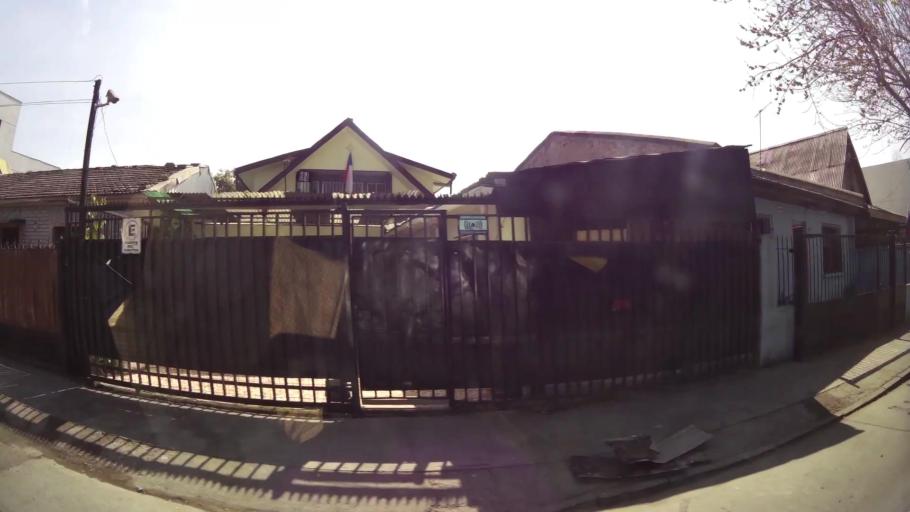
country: CL
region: Santiago Metropolitan
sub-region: Provincia de Santiago
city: Lo Prado
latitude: -33.4334
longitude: -70.7294
